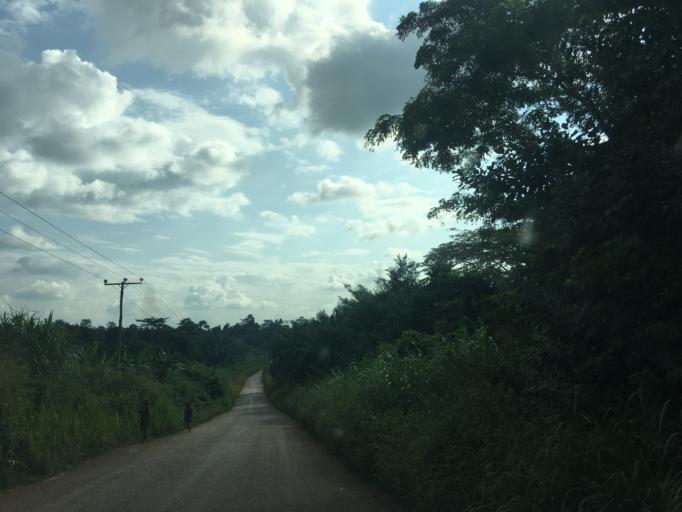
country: GH
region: Western
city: Bibiani
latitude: 6.7834
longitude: -2.5464
